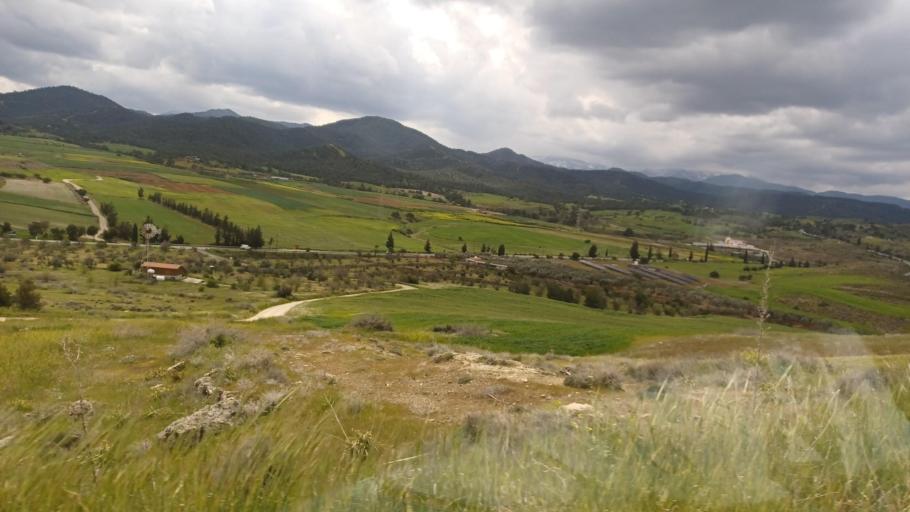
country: CY
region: Lefkosia
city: Astromeritis
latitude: 35.0897
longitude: 32.9585
